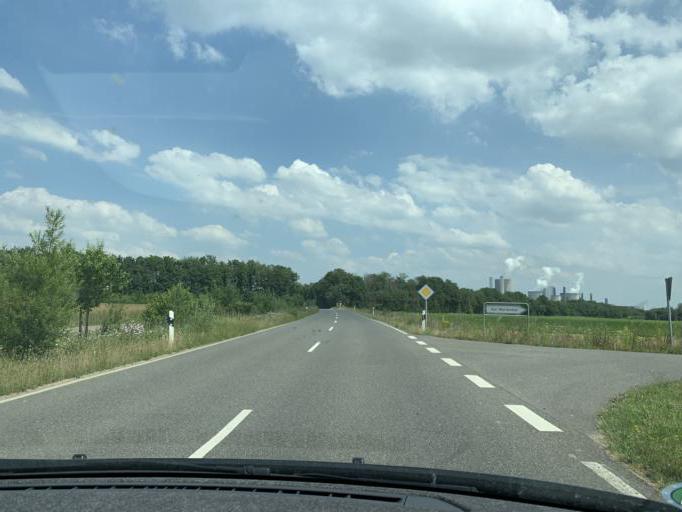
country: DE
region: North Rhine-Westphalia
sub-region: Regierungsbezirk Koln
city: Bergheim
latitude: 51.0023
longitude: 6.6282
